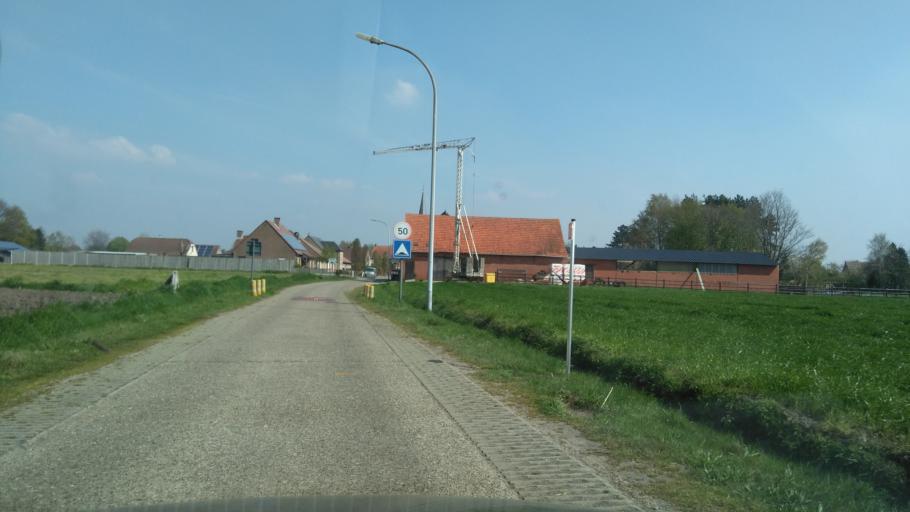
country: BE
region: Flanders
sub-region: Provincie Antwerpen
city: Baarle-Hertog
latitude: 51.4073
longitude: 4.8894
